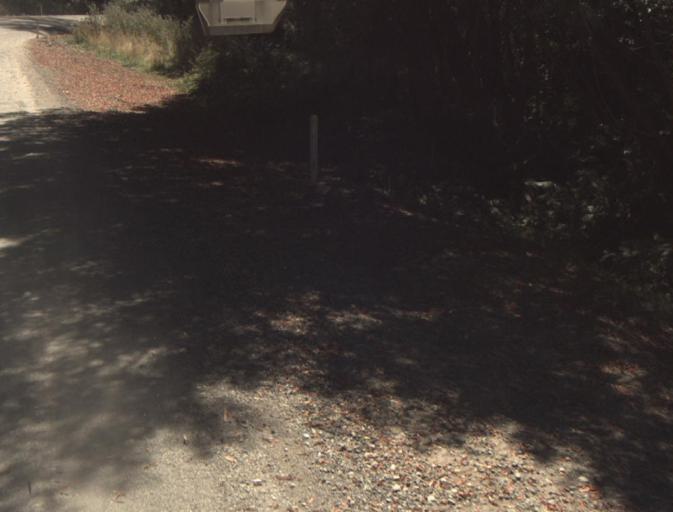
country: AU
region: Tasmania
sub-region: Dorset
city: Scottsdale
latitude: -41.2912
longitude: 147.3927
